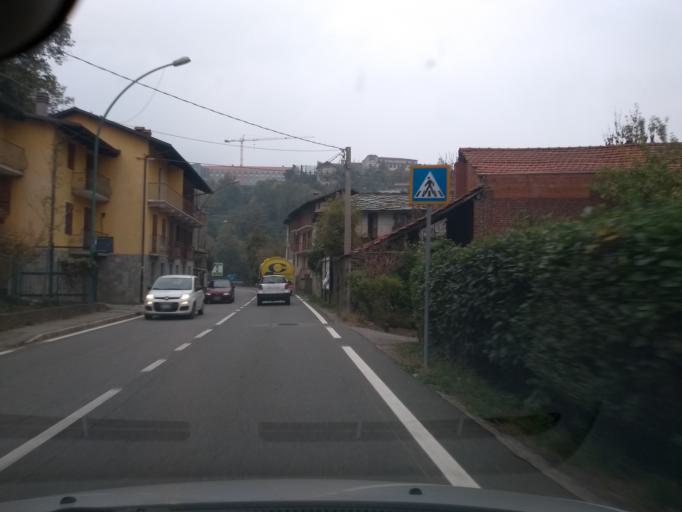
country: IT
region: Piedmont
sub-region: Provincia di Torino
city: Germagnano
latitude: 45.2681
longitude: 7.4763
